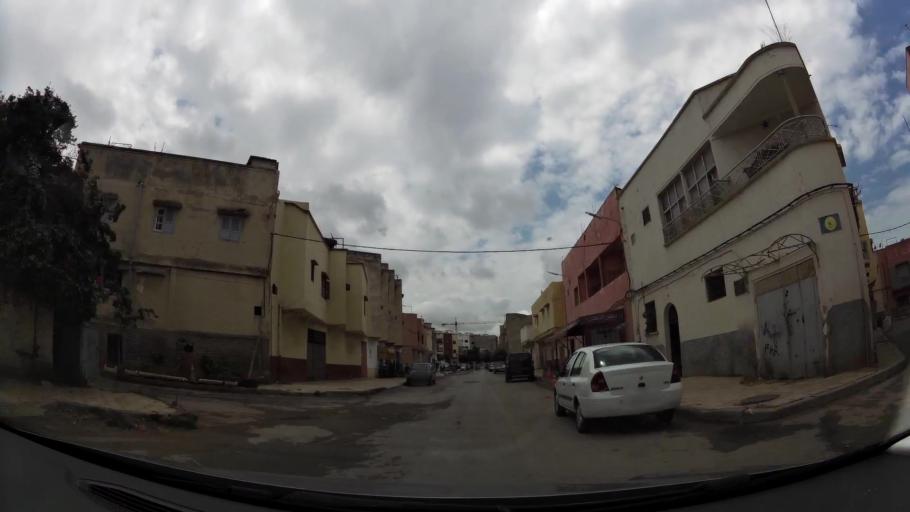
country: MA
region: Rabat-Sale-Zemmour-Zaer
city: Sale
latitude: 34.0388
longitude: -6.8110
